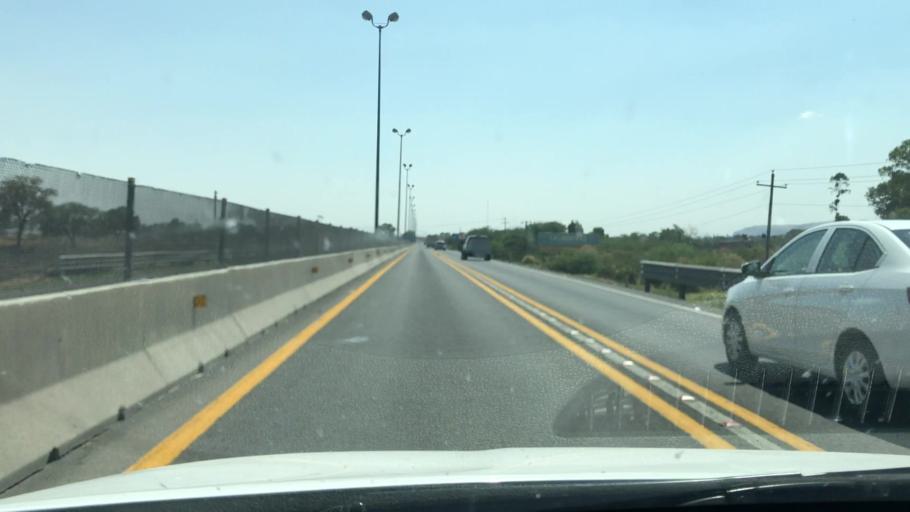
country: MX
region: Guanajuato
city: Abasolo
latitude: 20.4548
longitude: -101.5418
